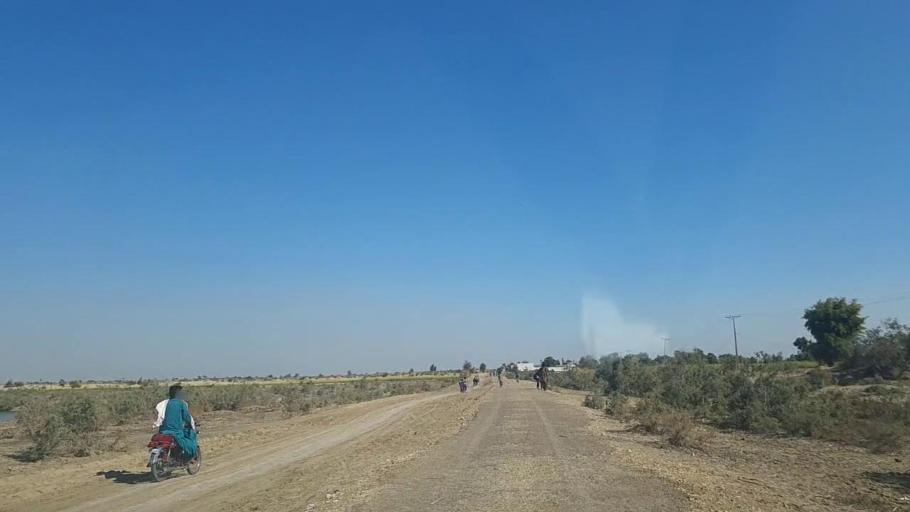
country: PK
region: Sindh
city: Sanghar
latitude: 26.2091
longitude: 68.8887
